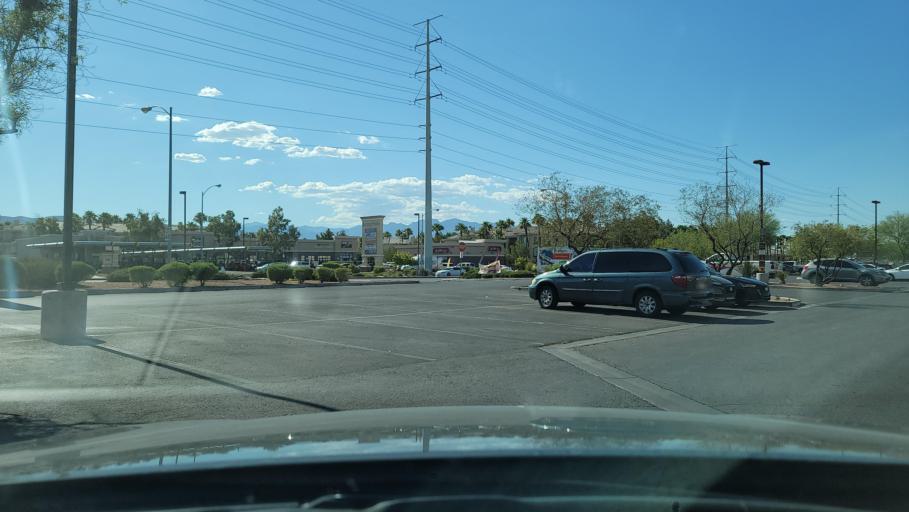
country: US
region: Nevada
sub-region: Clark County
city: Enterprise
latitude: 36.0562
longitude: -115.2786
